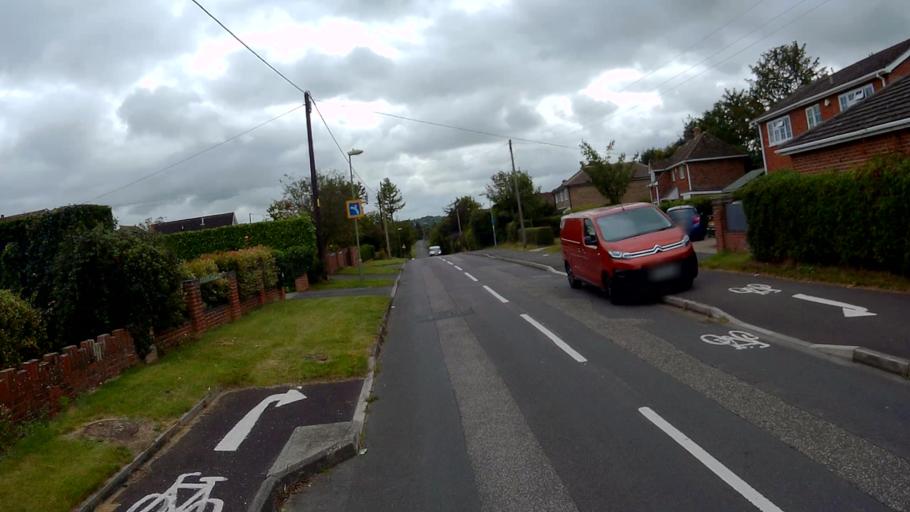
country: GB
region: England
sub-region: Hampshire
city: Basingstoke
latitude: 51.2568
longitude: -1.1379
